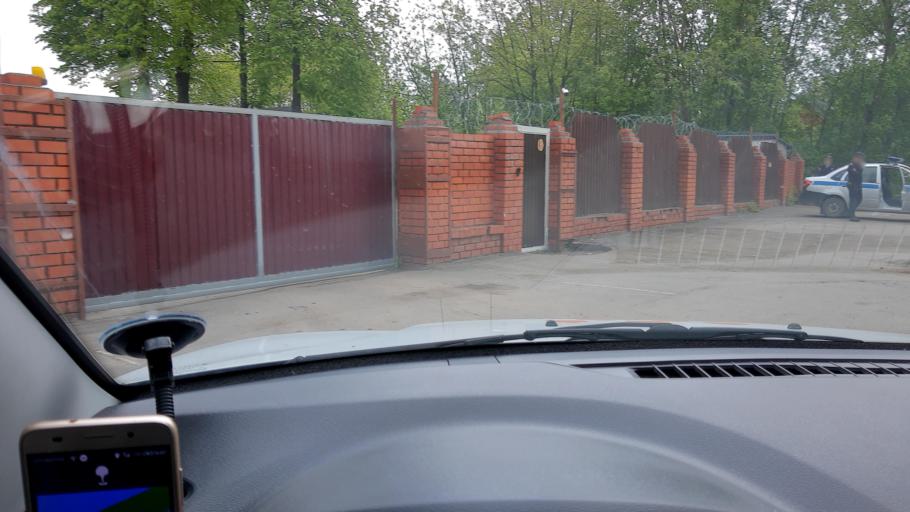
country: RU
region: Nizjnij Novgorod
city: Nizhniy Novgorod
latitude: 56.2799
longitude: 43.9562
